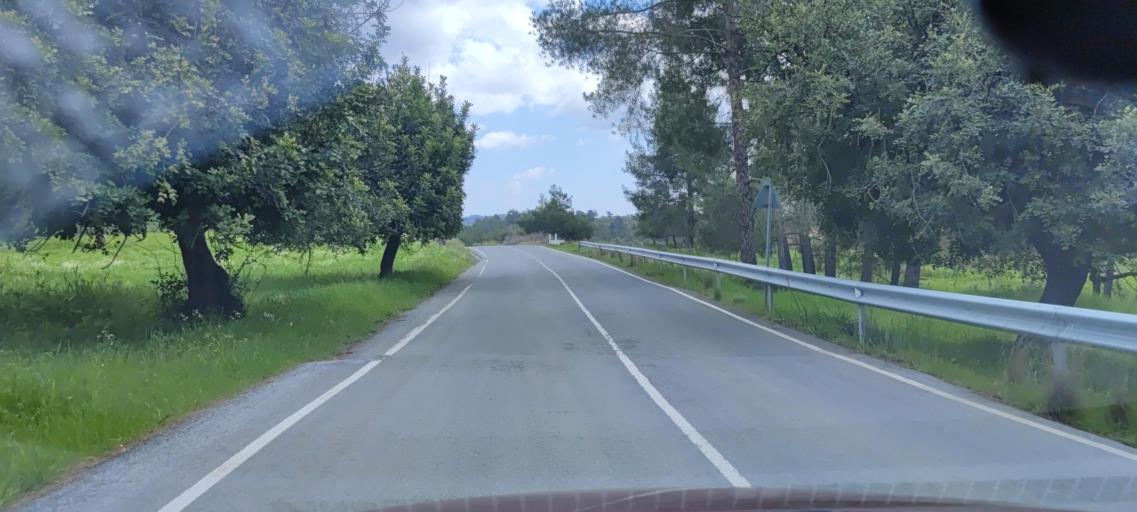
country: CY
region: Larnaka
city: Kornos
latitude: 34.9190
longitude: 33.3540
